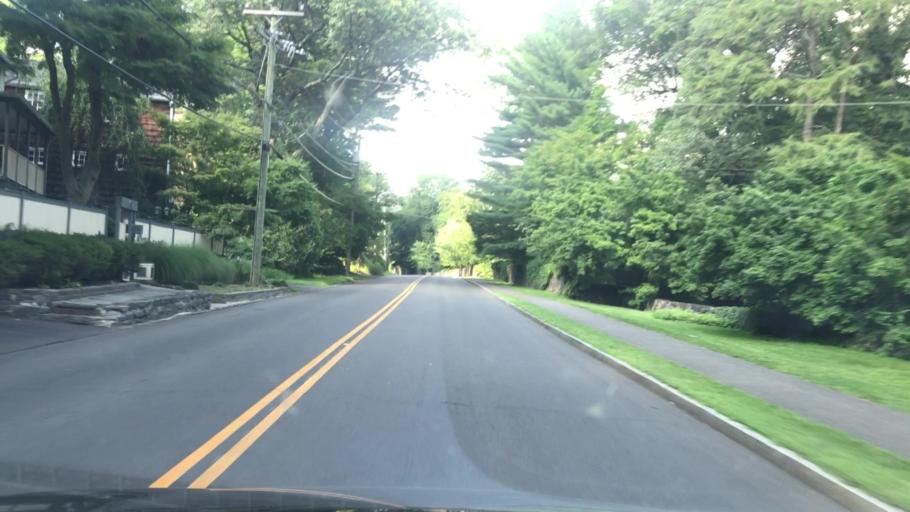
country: US
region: Connecticut
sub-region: Fairfield County
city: Byram
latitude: 41.0052
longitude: -73.6473
